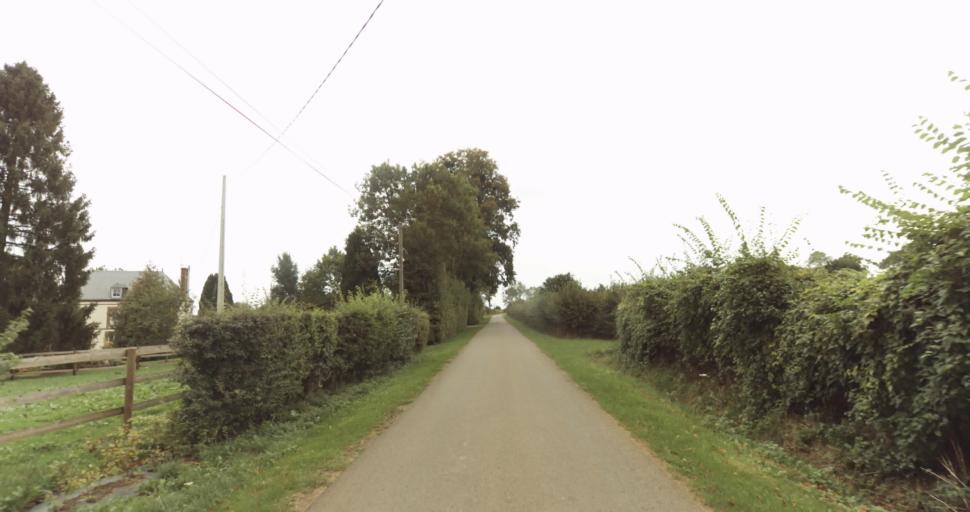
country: FR
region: Lower Normandy
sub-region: Departement de l'Orne
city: Gace
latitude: 48.7282
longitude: 0.3261
